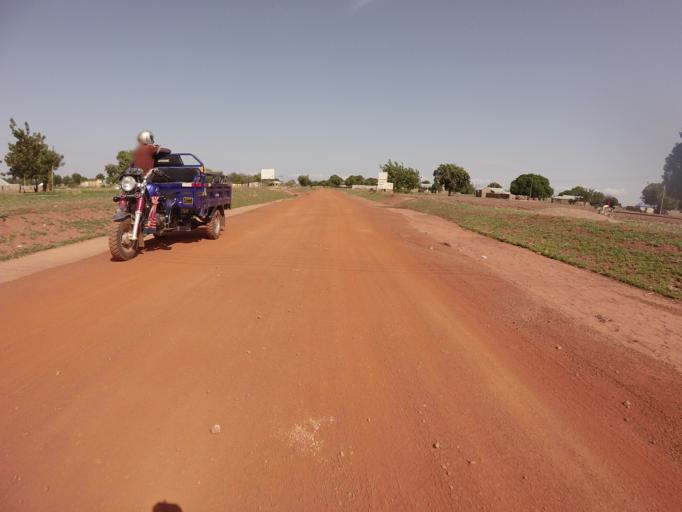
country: GH
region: Upper East
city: Bawku
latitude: 10.8373
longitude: -0.1768
